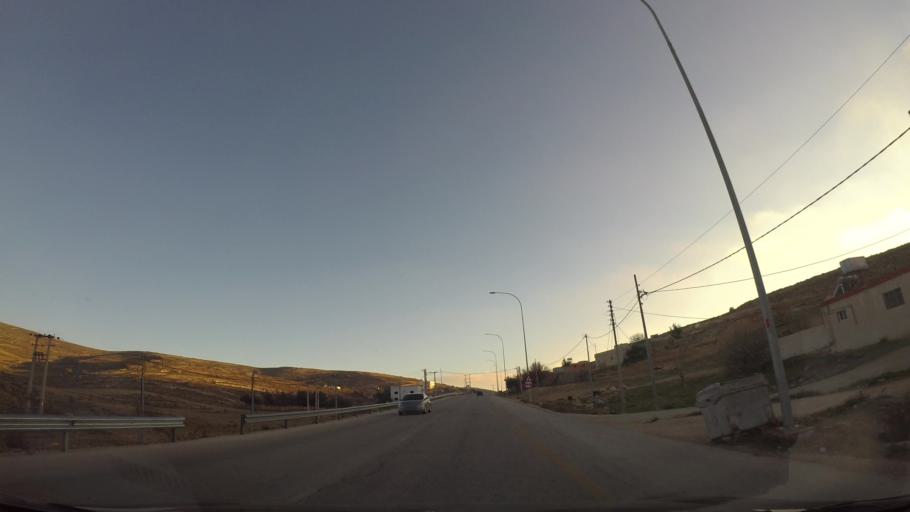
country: JO
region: Ma'an
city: Petra
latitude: 30.4239
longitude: 35.5129
